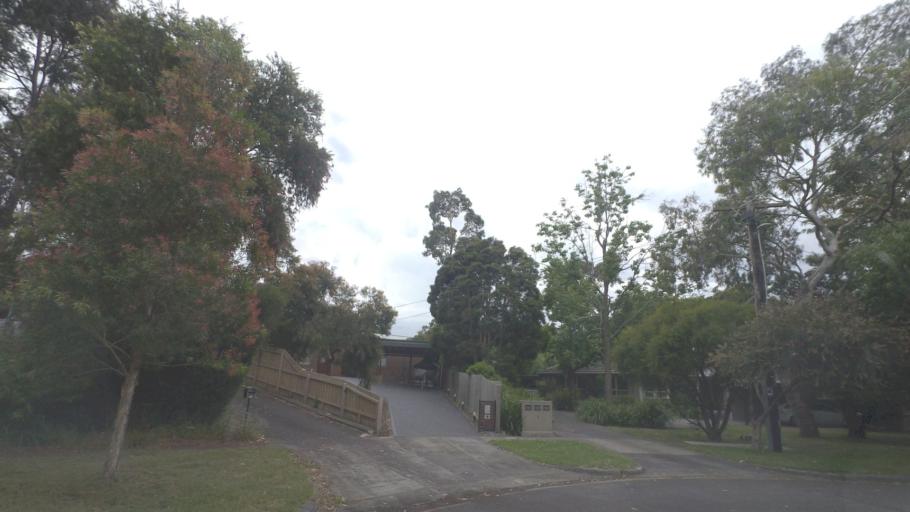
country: AU
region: Victoria
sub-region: Maroondah
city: Croydon North
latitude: -37.7871
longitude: 145.2990
